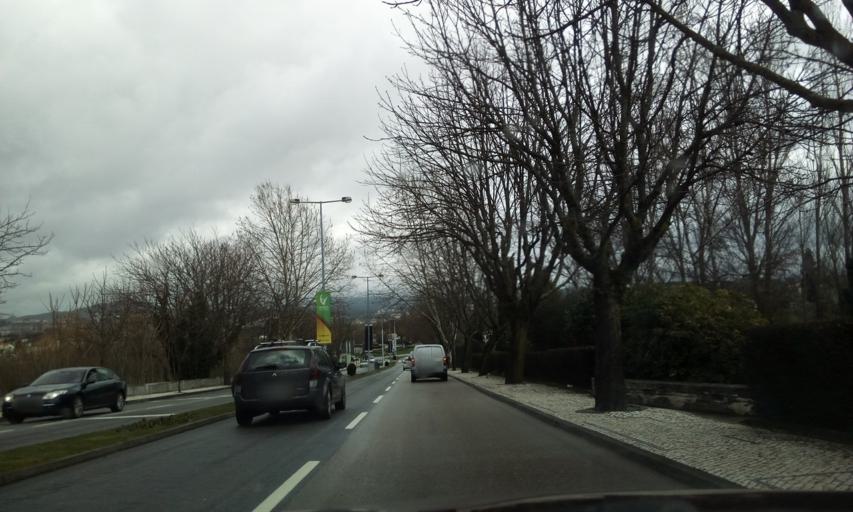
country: PT
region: Viseu
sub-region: Viseu
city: Viseu
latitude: 40.6603
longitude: -7.9054
